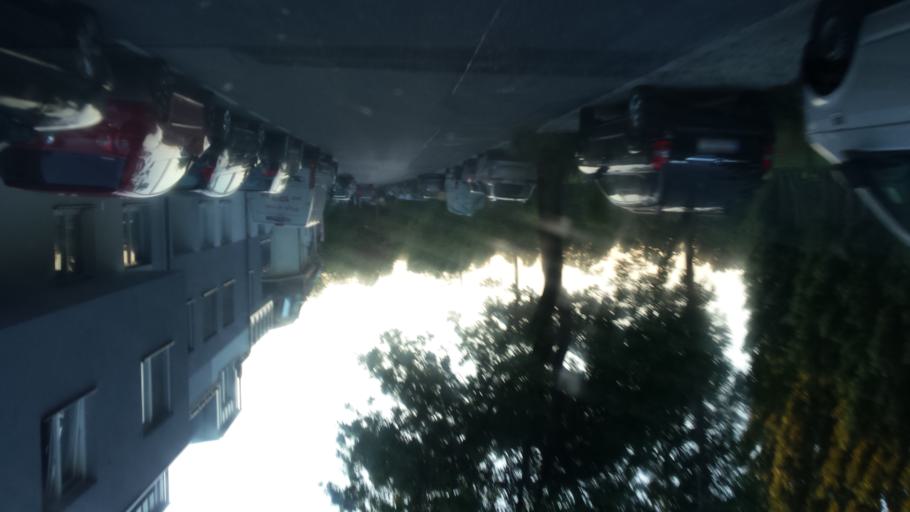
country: AT
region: Lower Austria
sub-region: Politischer Bezirk Wien-Umgebung
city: Schwechat
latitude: 48.1731
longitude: 16.4253
